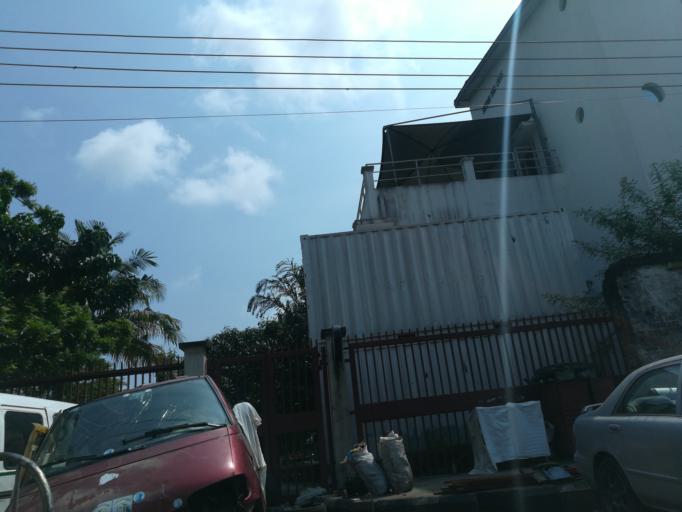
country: NG
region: Lagos
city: Lagos
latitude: 6.4493
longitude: 3.3969
